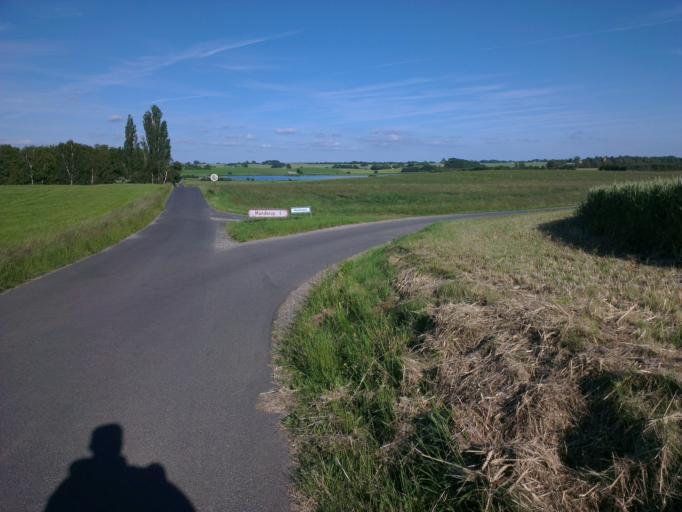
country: DK
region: Capital Region
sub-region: Frederikssund Kommune
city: Skibby
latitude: 55.7565
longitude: 11.9844
